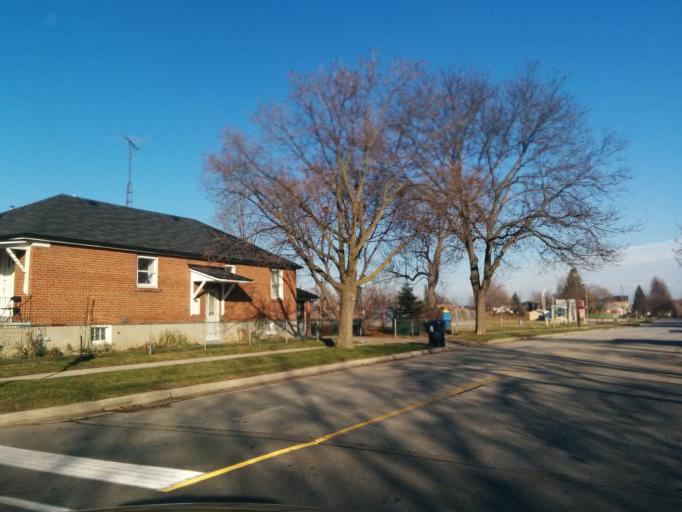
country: CA
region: Ontario
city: Etobicoke
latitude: 43.6086
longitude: -79.5355
